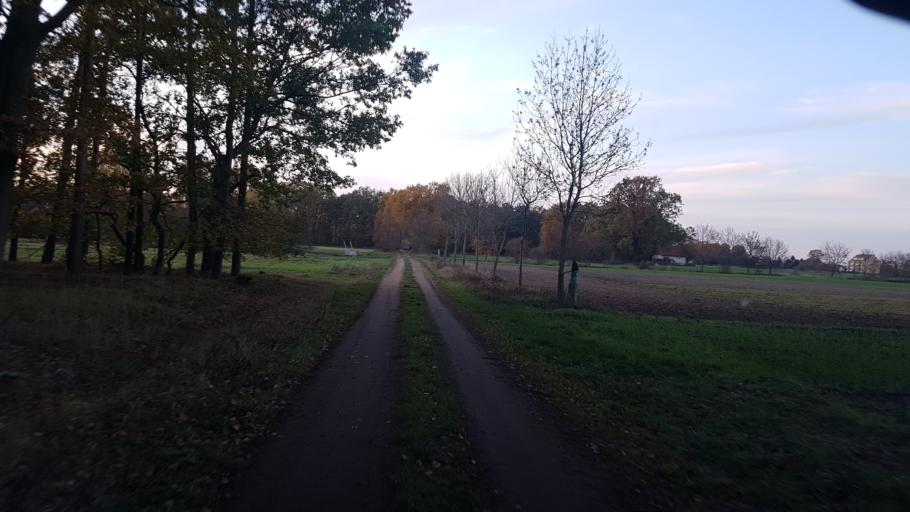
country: DE
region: Brandenburg
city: Schilda
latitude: 51.5919
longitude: 13.3159
